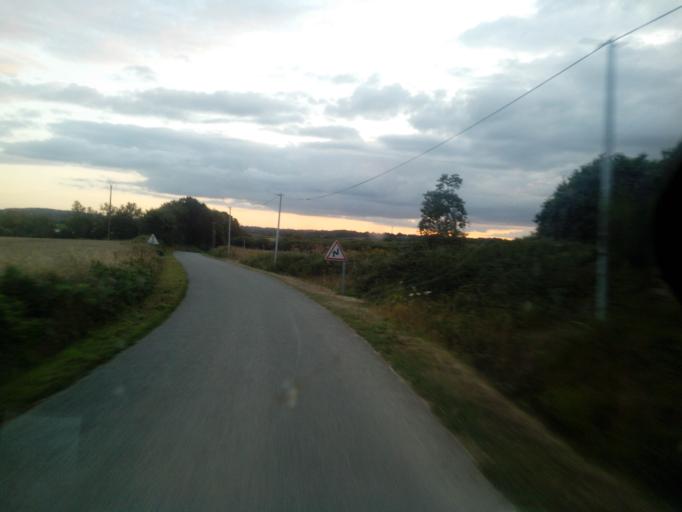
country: FR
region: Brittany
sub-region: Departement du Morbihan
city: Guegon
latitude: 47.9048
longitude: -2.6168
